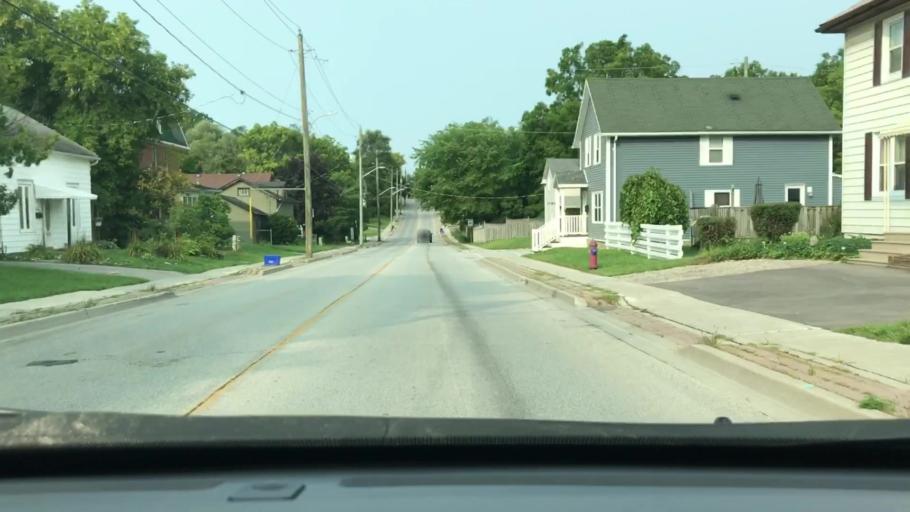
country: CA
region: Ontario
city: Newmarket
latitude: 44.0523
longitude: -79.4493
